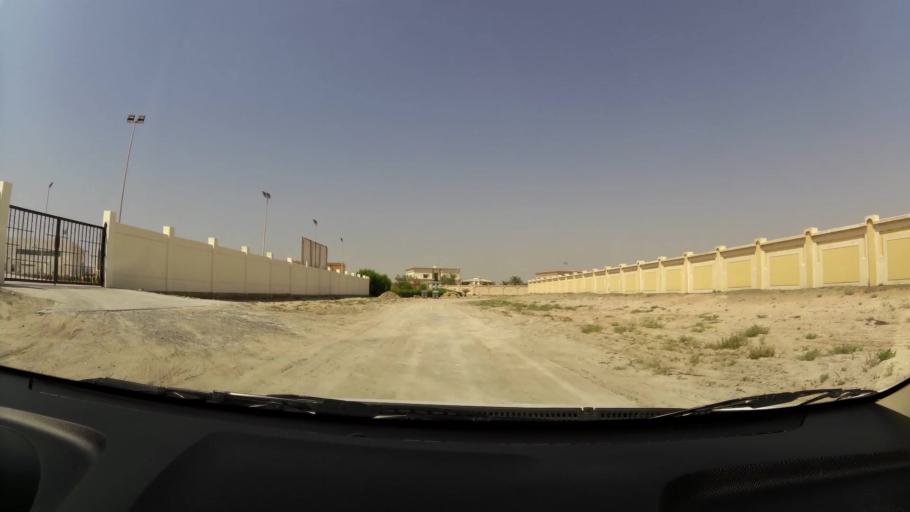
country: AE
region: Ajman
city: Ajman
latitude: 25.4184
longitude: 55.4761
